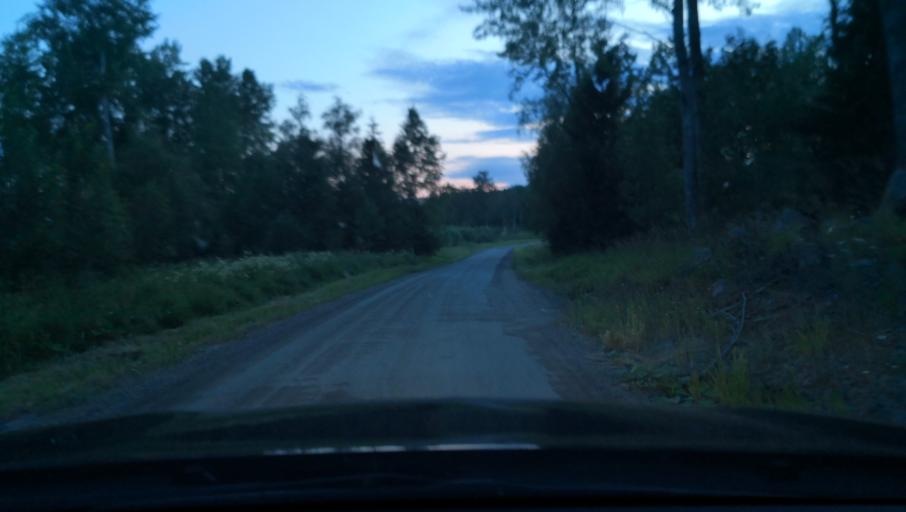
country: SE
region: Uppsala
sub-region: Osthammars Kommun
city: Bjorklinge
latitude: 60.0035
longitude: 17.3438
